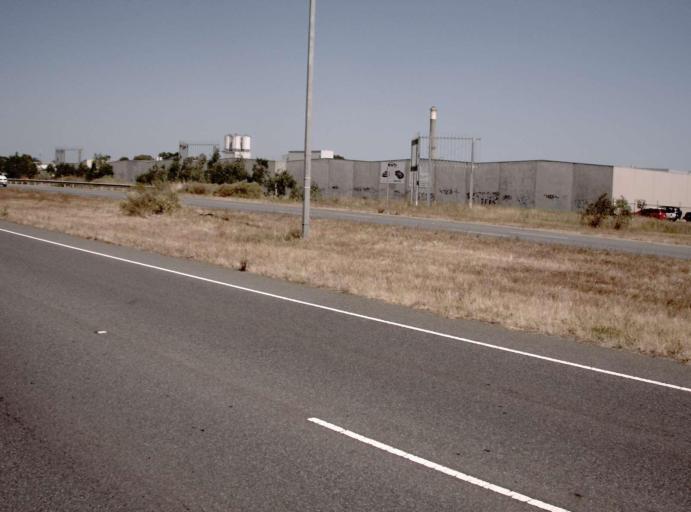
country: AU
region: Victoria
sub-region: Casey
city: Doveton
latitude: -38.0043
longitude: 145.2195
